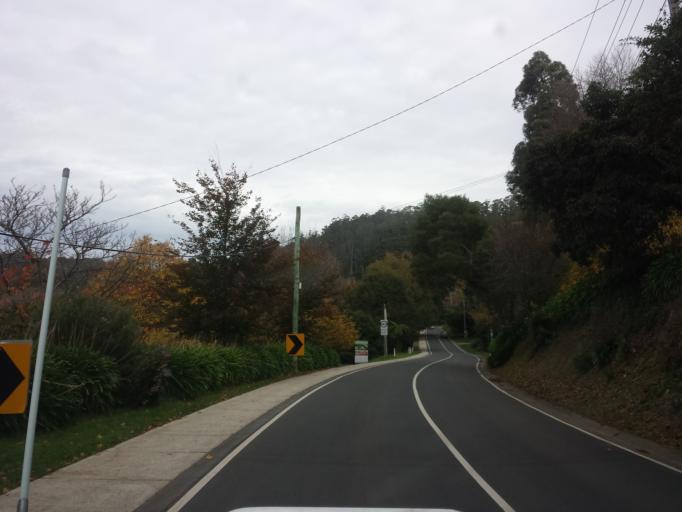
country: AU
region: Victoria
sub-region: Yarra Ranges
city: Monbulk
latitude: -37.8876
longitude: 145.3925
